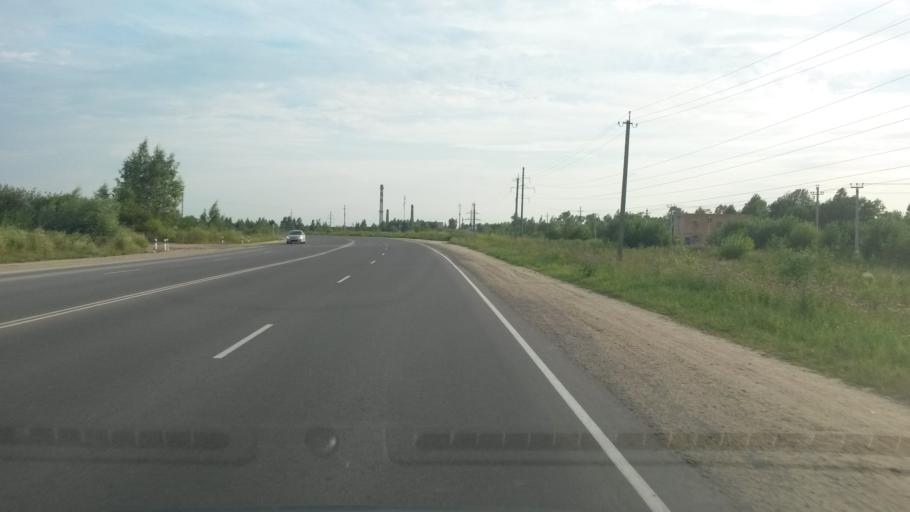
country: RU
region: Ivanovo
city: Novo-Talitsy
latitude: 57.0113
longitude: 40.8790
